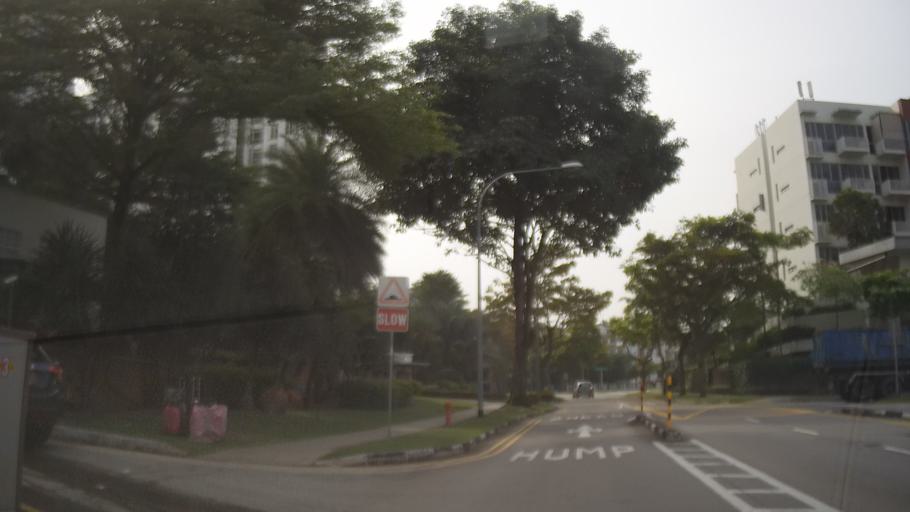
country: MY
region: Johor
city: Johor Bahru
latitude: 1.4309
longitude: 103.7849
